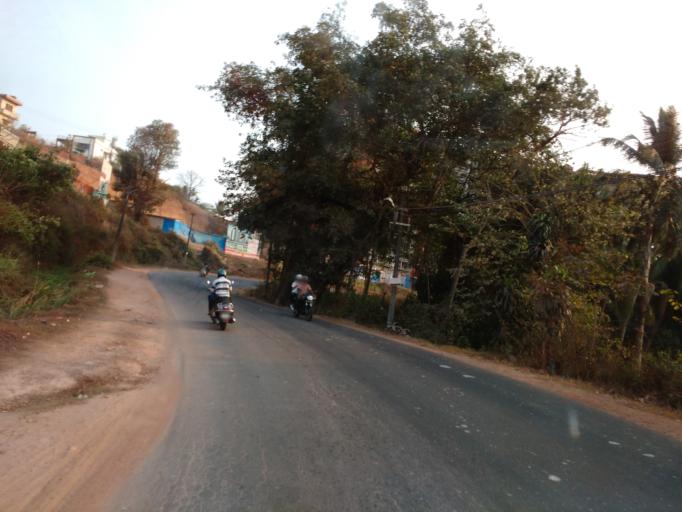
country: IN
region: Karnataka
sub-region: Dakshina Kannada
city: Mangalore
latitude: 12.8941
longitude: 74.8898
